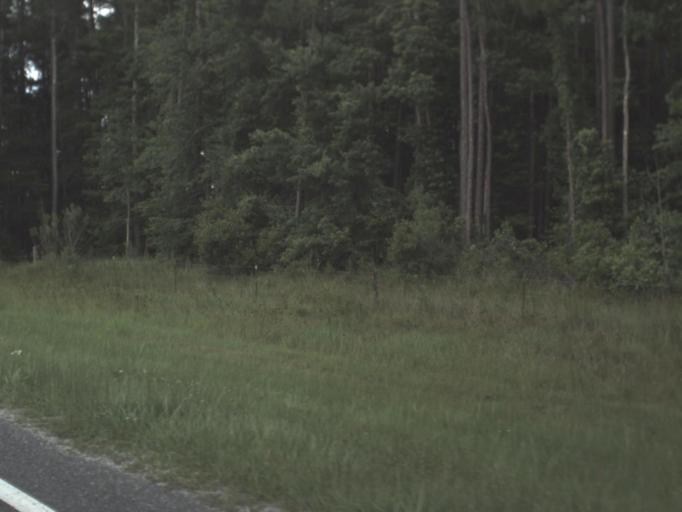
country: US
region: Florida
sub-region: Clay County
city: Middleburg
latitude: 29.9967
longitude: -81.8977
